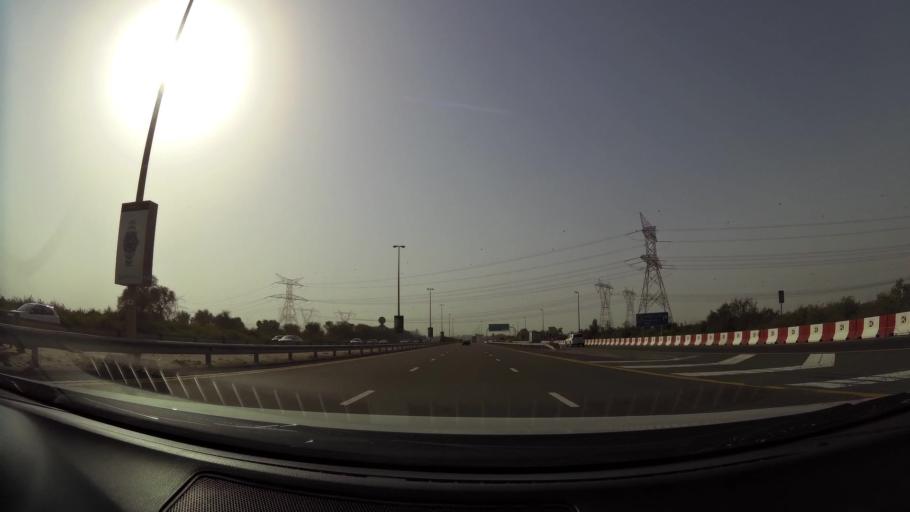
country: AE
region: Dubai
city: Dubai
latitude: 25.1662
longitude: 55.3276
